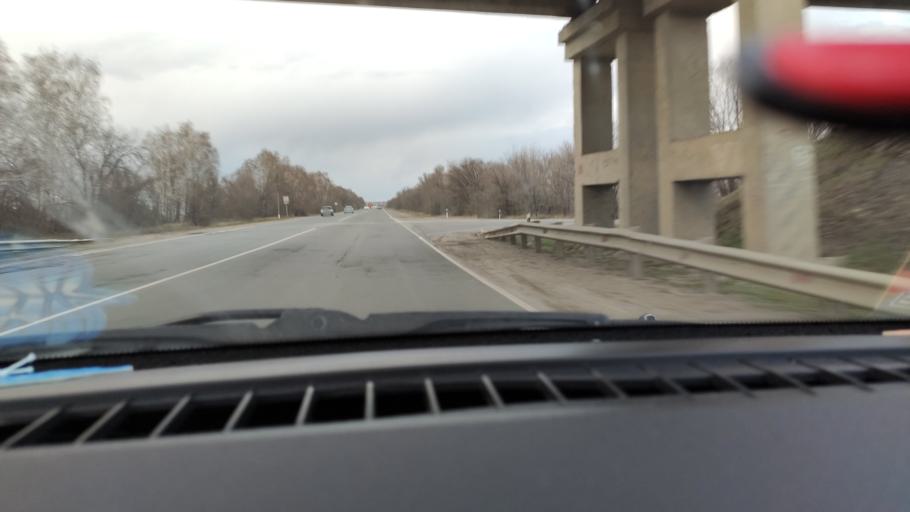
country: RU
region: Saratov
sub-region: Saratovskiy Rayon
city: Saratov
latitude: 51.7010
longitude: 46.0113
